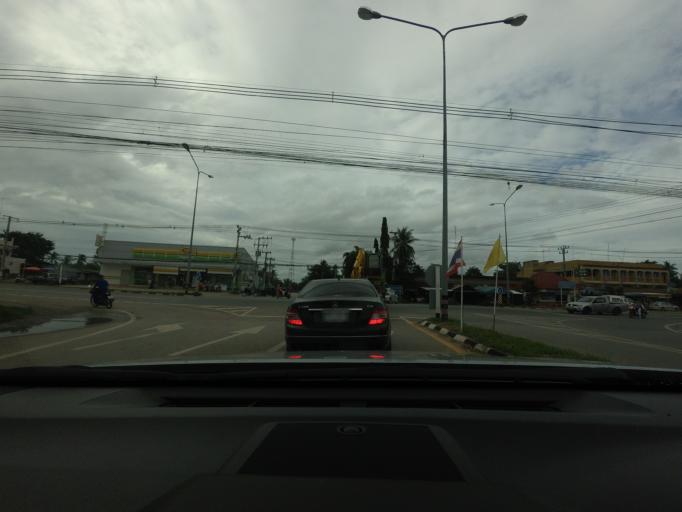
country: TH
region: Prachuap Khiri Khan
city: Hua Hin
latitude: 12.5834
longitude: 99.8415
